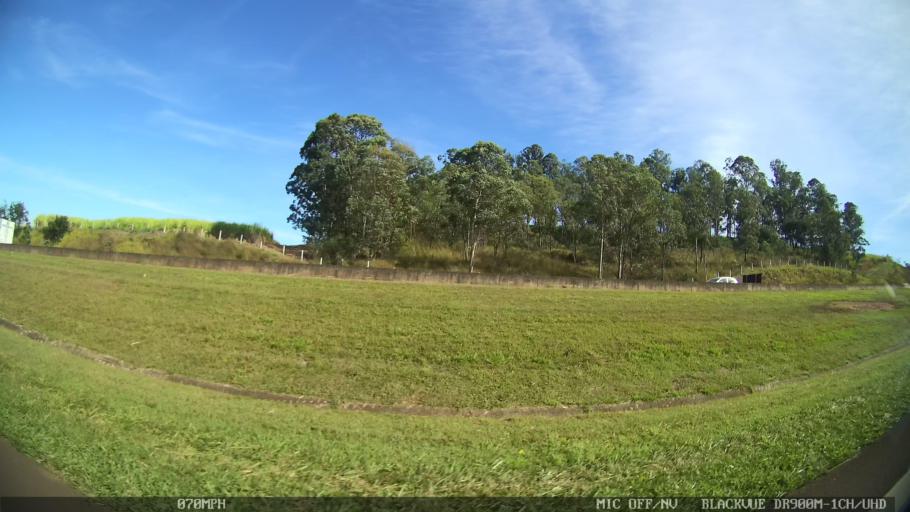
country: BR
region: Sao Paulo
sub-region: Araras
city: Araras
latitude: -22.3333
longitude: -47.3891
